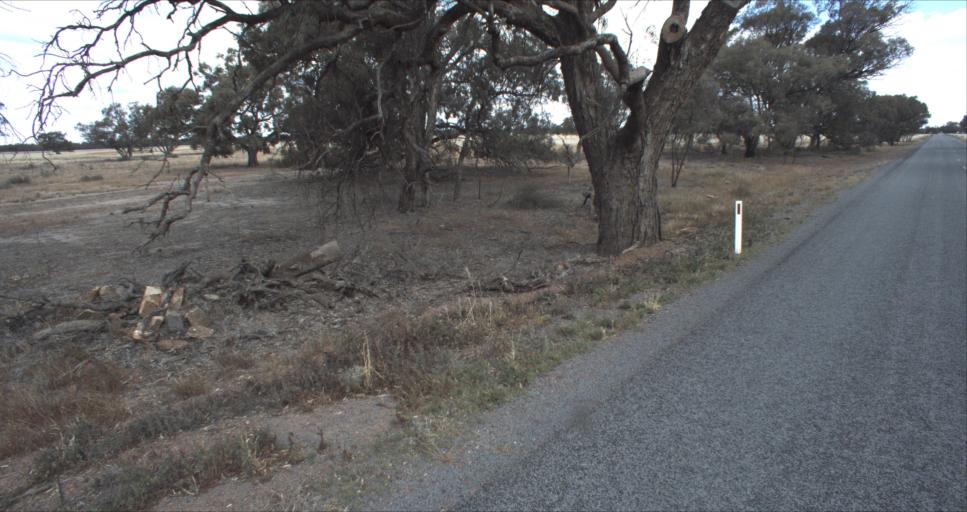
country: AU
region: New South Wales
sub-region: Leeton
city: Leeton
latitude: -34.6914
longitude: 146.3437
